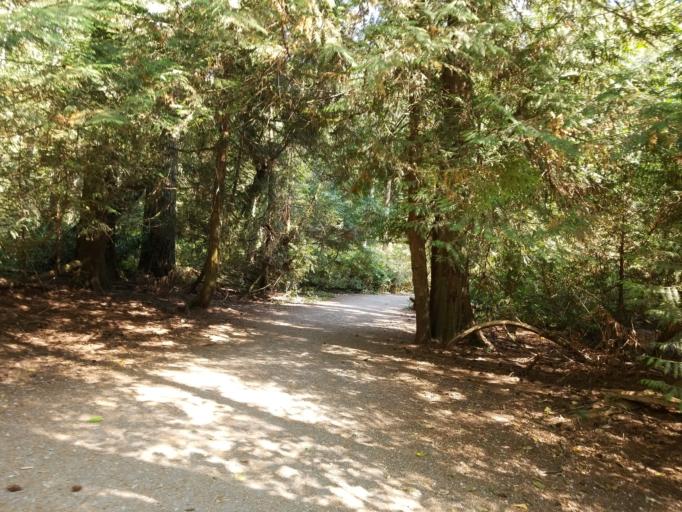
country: CA
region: British Columbia
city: West End
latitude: 49.2520
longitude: -123.2132
